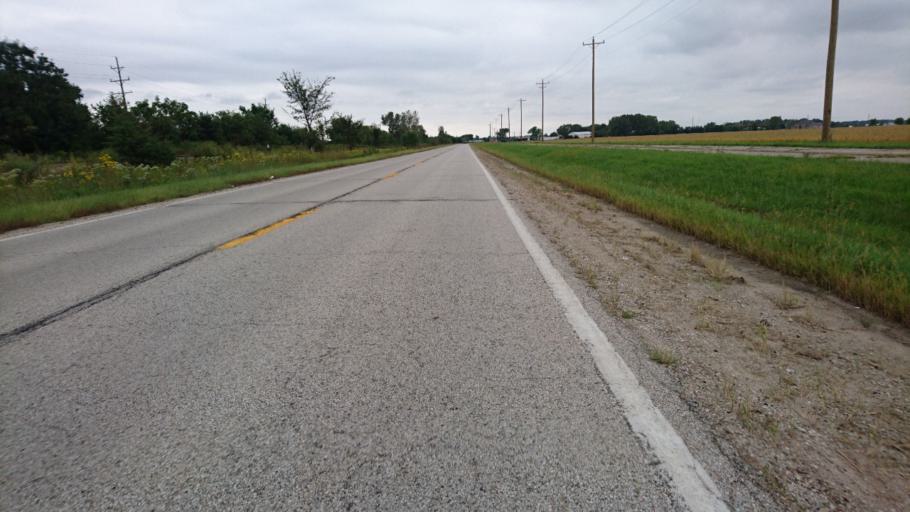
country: US
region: Illinois
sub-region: Livingston County
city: Pontiac
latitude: 40.9055
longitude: -88.6165
